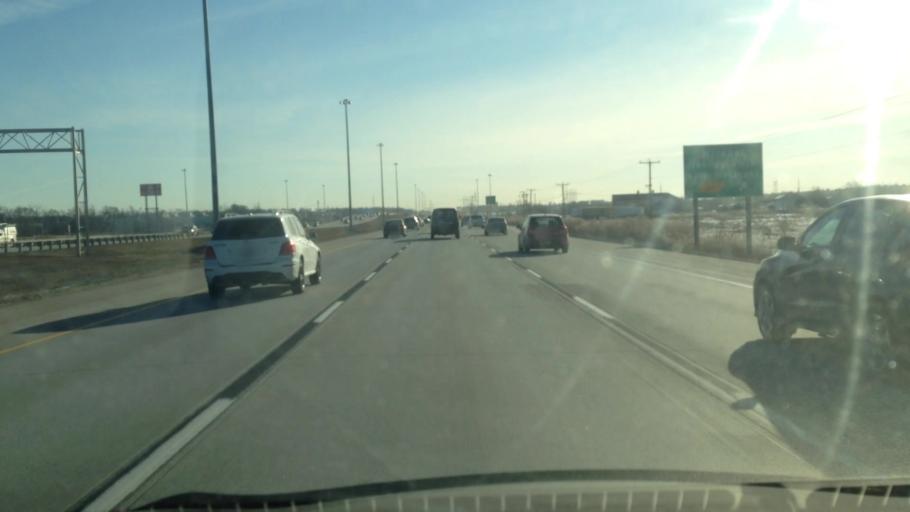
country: CA
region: Quebec
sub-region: Laurentides
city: Blainville
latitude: 45.6969
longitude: -73.9442
